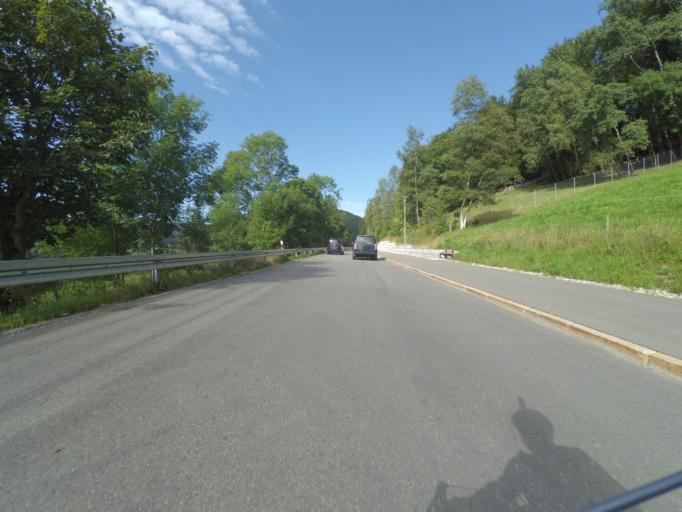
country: DE
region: Baden-Wuerttemberg
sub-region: Freiburg Region
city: Hinterzarten
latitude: 47.8883
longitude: 8.1269
